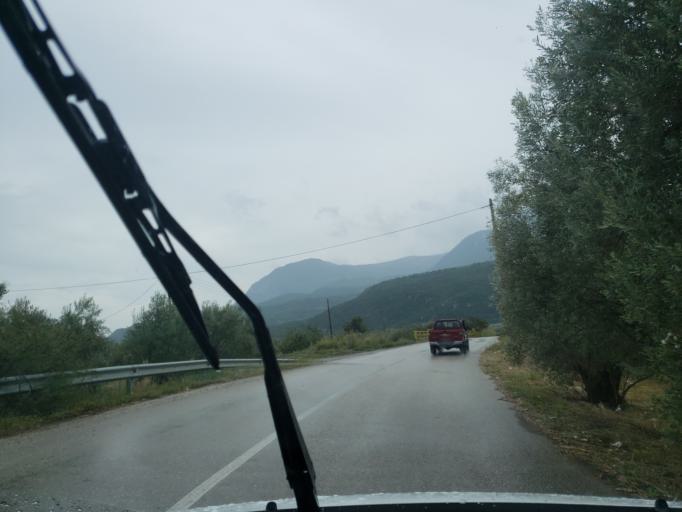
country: GR
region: Central Greece
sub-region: Nomos Fthiotidos
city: Anthili
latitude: 38.8010
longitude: 22.4635
